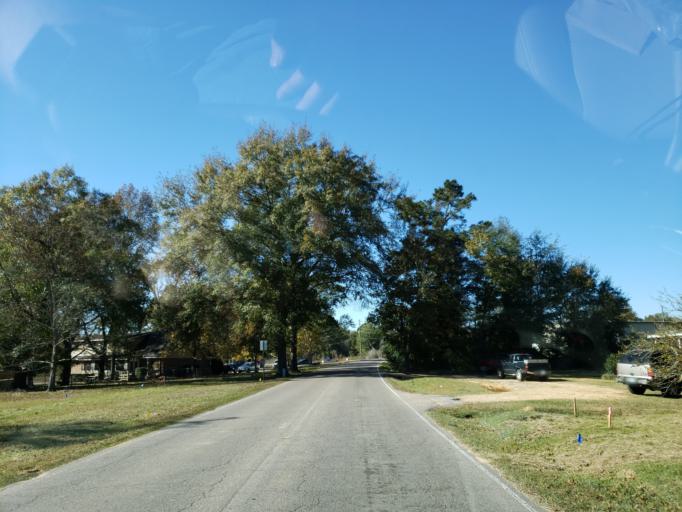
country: US
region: Mississippi
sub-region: Lamar County
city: West Hattiesburg
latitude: 31.3105
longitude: -89.3976
